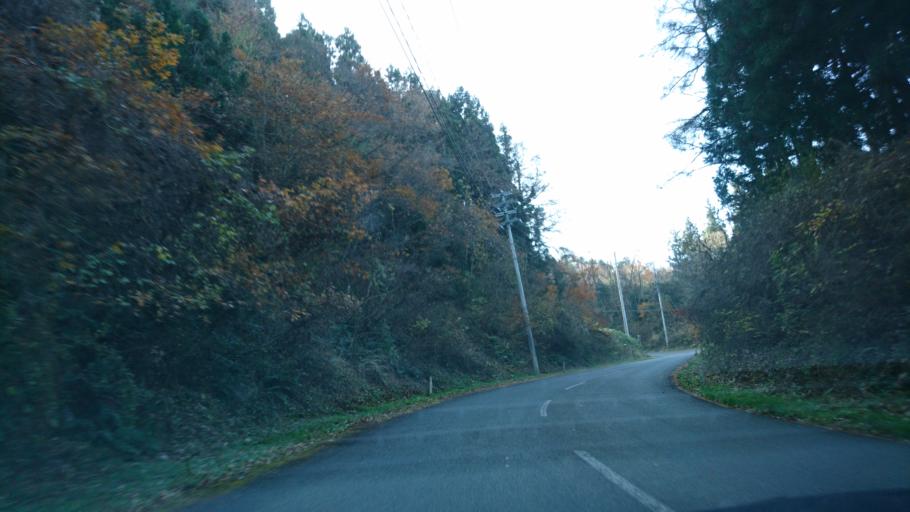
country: JP
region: Iwate
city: Ichinoseki
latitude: 38.8629
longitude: 141.3401
